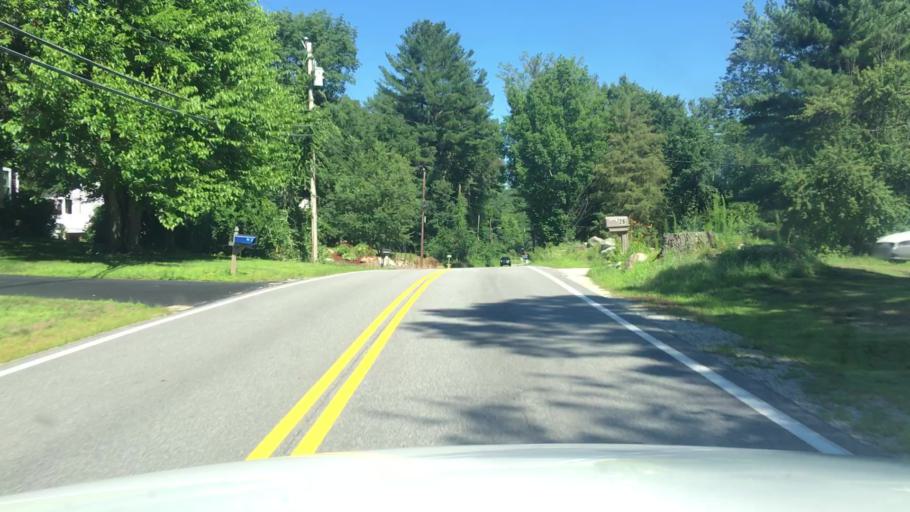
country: US
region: New Hampshire
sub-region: Merrimack County
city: South Hooksett
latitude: 43.0402
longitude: -71.4160
